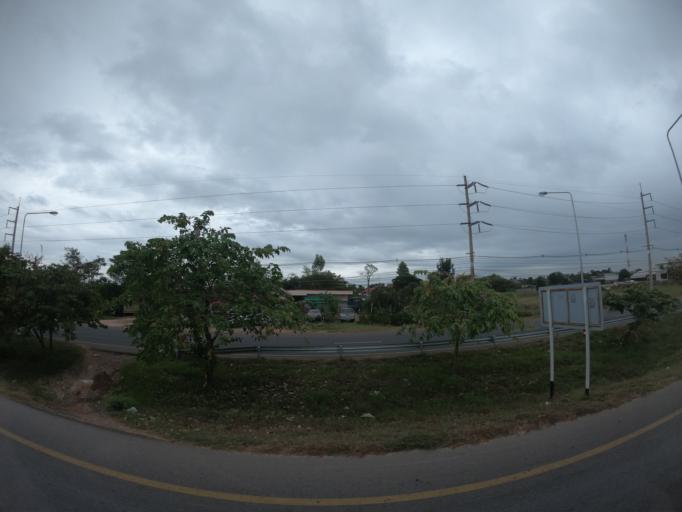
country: TH
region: Roi Et
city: Roi Et
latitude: 16.0519
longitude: 103.6204
